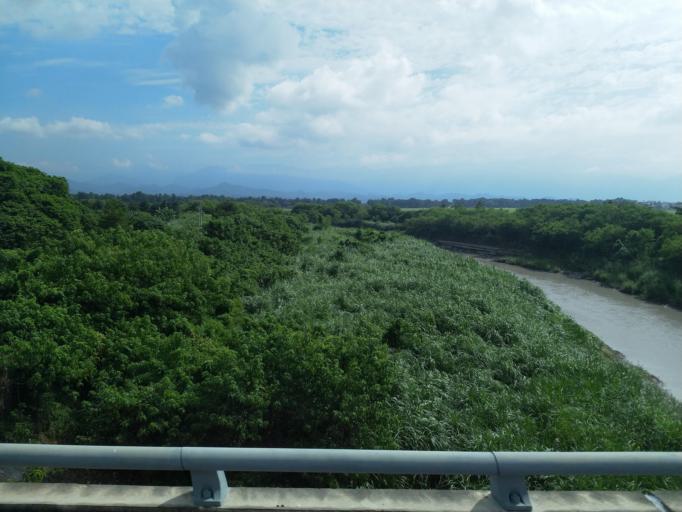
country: TW
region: Taiwan
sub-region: Pingtung
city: Pingtung
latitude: 22.8614
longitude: 120.4916
